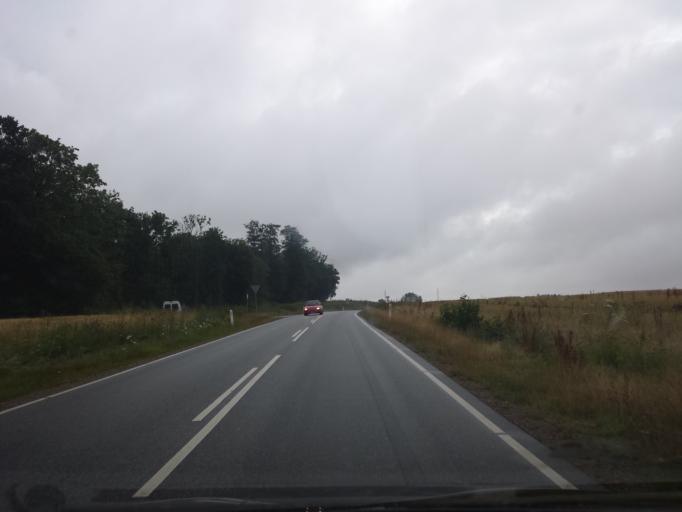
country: DK
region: South Denmark
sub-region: Sonderborg Kommune
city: Grasten
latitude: 54.9481
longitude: 9.6344
